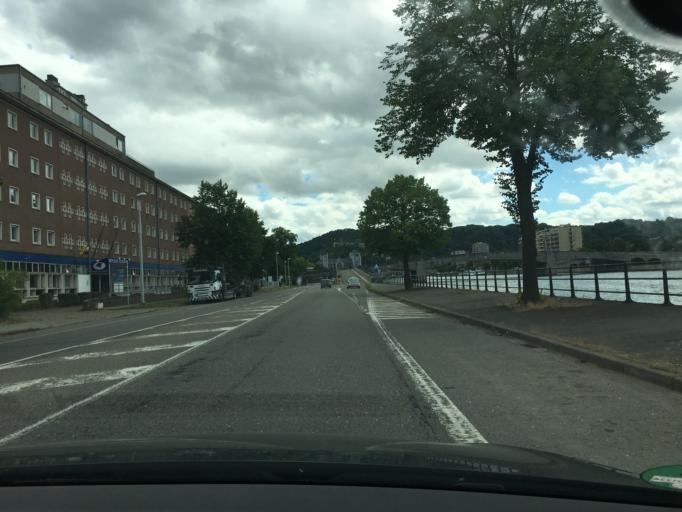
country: BE
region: Wallonia
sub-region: Province de Liege
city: Huy
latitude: 50.5275
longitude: 5.2423
